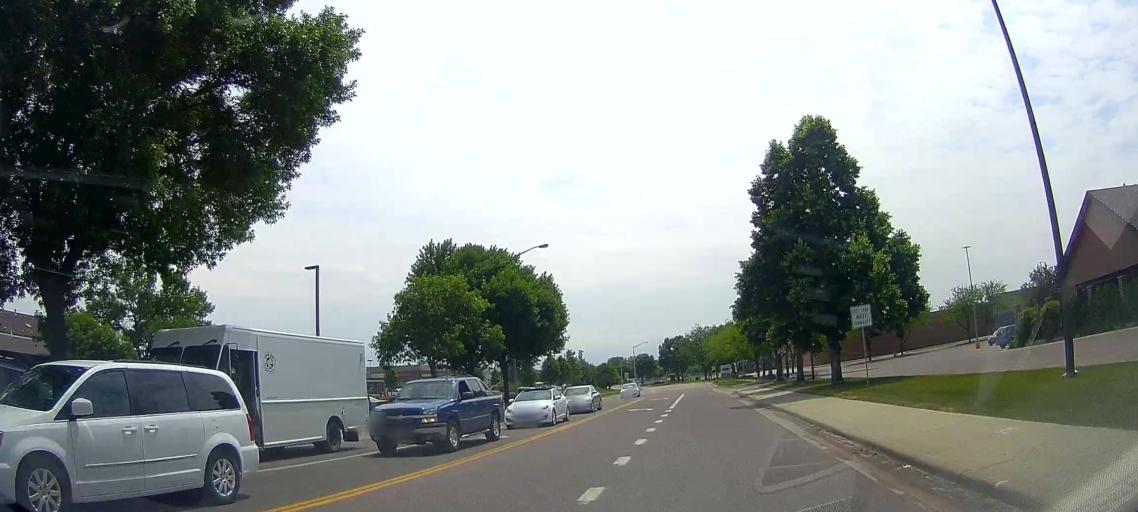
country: US
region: South Dakota
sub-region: Minnehaha County
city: Sioux Falls
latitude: 43.5147
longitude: -96.7413
